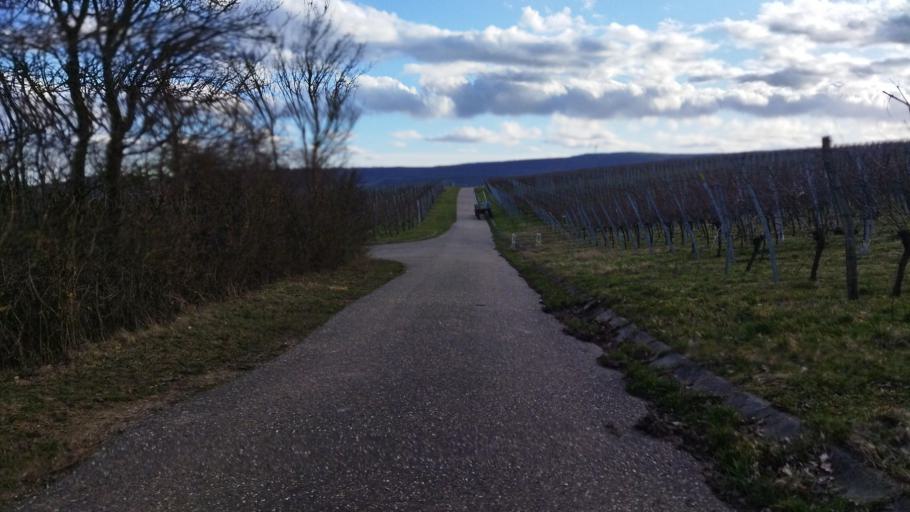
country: DE
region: Baden-Wuerttemberg
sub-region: Regierungsbezirk Stuttgart
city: Guglingen
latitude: 49.0802
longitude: 9.0065
